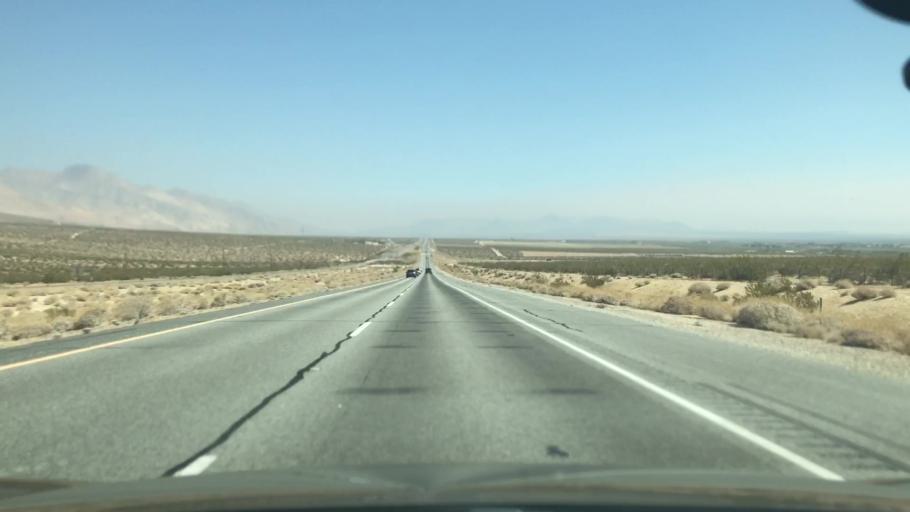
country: US
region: California
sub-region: Kern County
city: Inyokern
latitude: 35.6852
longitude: -117.8668
